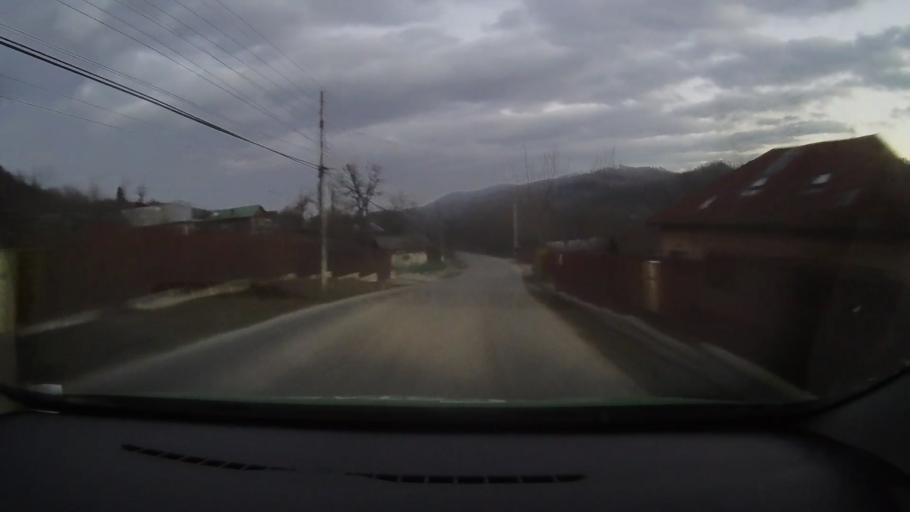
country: RO
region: Prahova
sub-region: Comuna Provita de Sus
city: Provita de Sus
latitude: 45.1340
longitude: 25.6408
